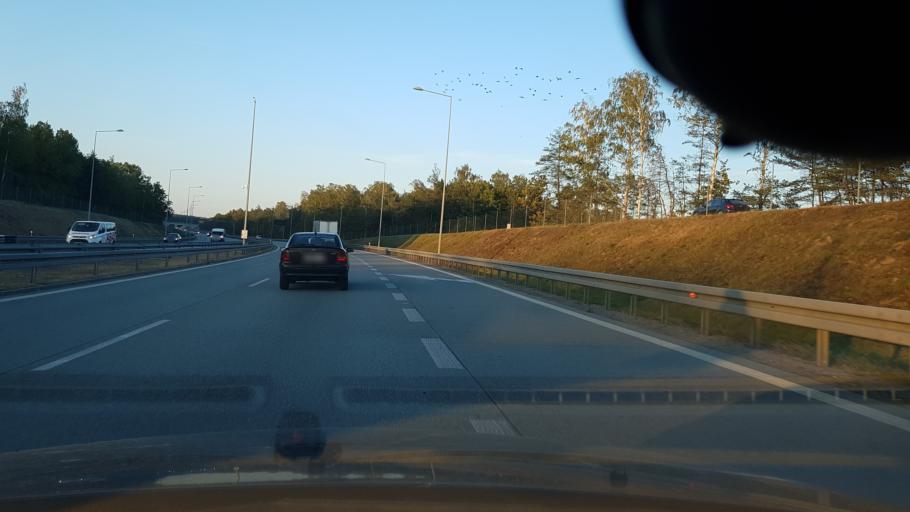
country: PL
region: Lodz Voivodeship
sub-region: Powiat tomaszowski
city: Tomaszow Mazowiecki
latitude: 51.5664
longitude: 20.0232
